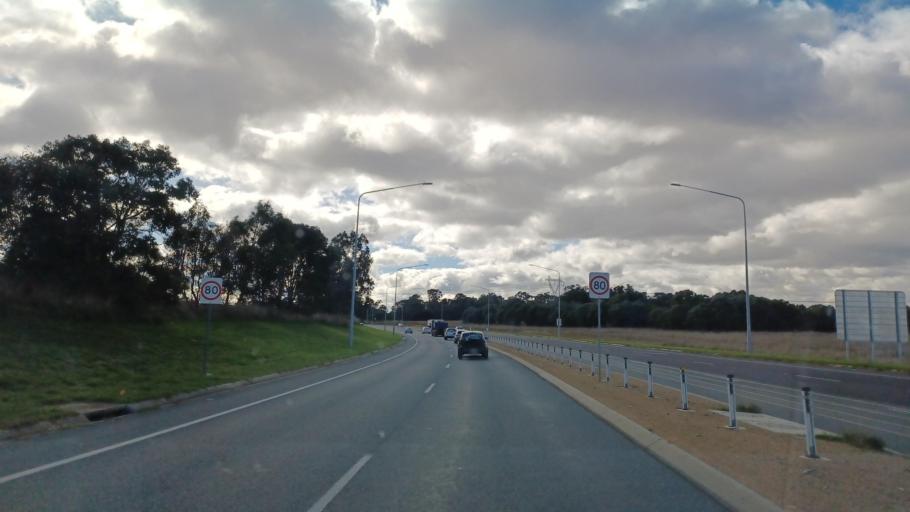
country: AU
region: Australian Capital Territory
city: Kaleen
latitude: -35.2233
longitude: 149.1273
